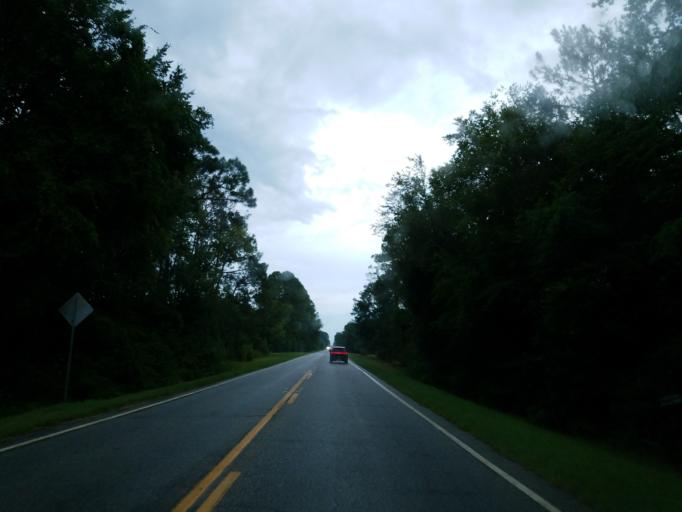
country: US
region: Georgia
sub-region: Berrien County
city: Ray City
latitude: 31.0744
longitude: -83.1875
